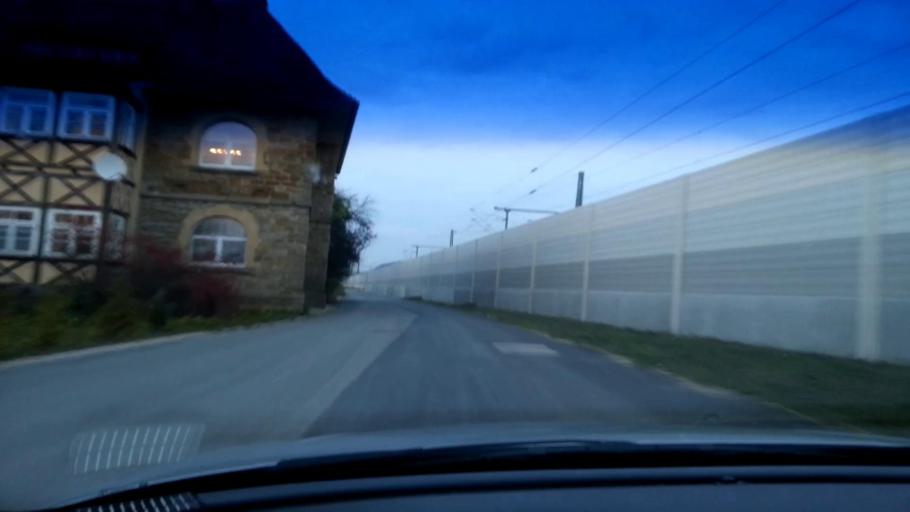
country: DE
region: Bavaria
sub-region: Upper Franconia
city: Zapfendorf
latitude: 50.0195
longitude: 10.9307
